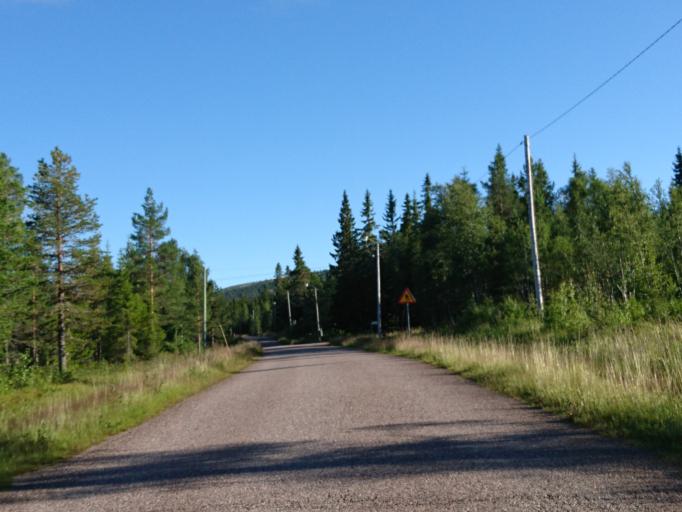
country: SE
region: Dalarna
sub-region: Malung-Saelens kommun
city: Malung
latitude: 61.1736
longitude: 13.1752
